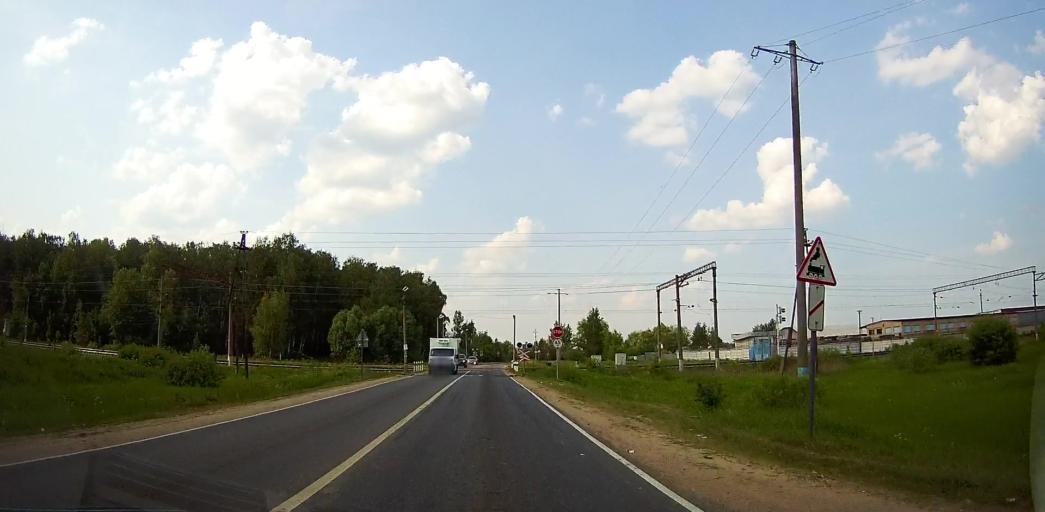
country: RU
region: Moskovskaya
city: Malino
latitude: 55.0551
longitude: 38.1420
